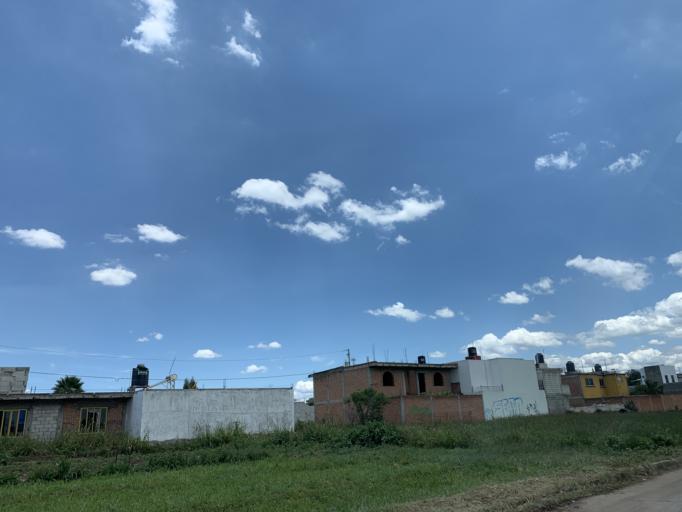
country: MX
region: Puebla
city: Cholula
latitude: 19.0756
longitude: -98.3264
